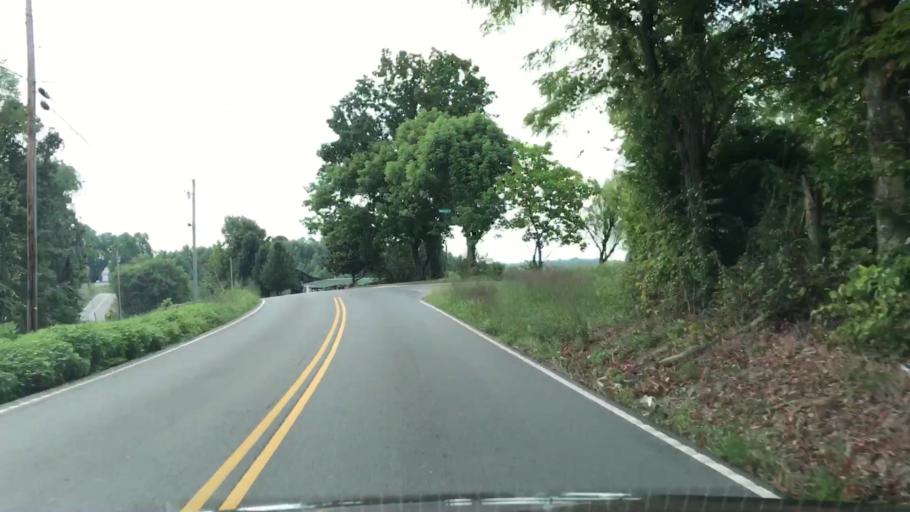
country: US
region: Tennessee
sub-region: Sumner County
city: Westmoreland
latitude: 36.5154
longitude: -86.1794
